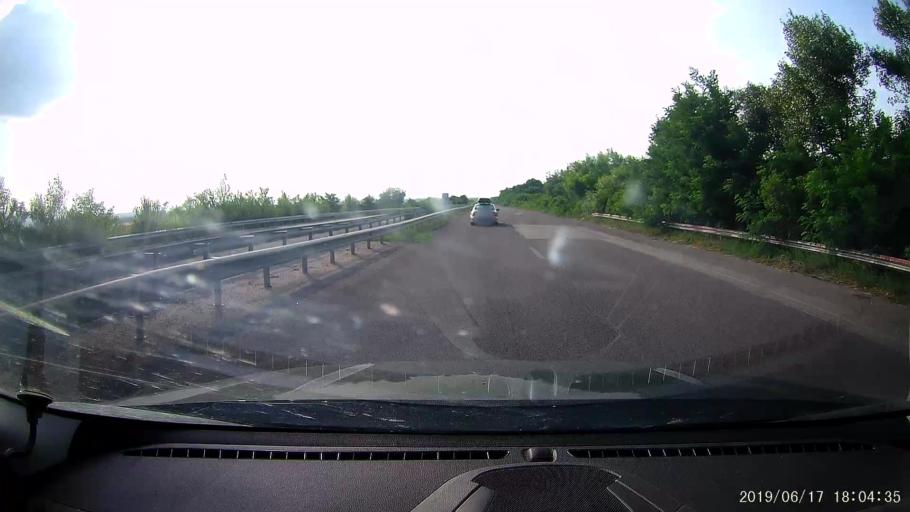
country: BG
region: Khaskovo
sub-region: Obshtina Svilengrad
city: Svilengrad
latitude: 41.7873
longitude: 26.1952
